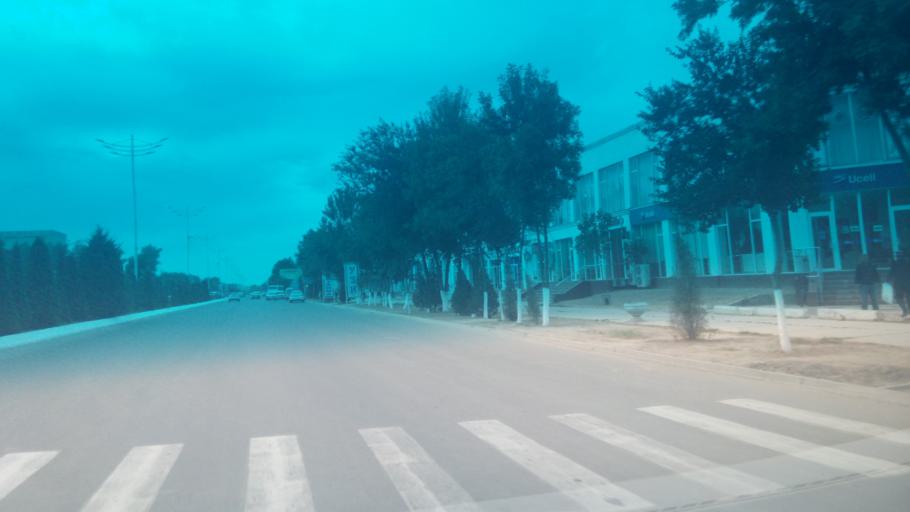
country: UZ
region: Sirdaryo
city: Guliston
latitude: 40.4972
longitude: 68.7747
